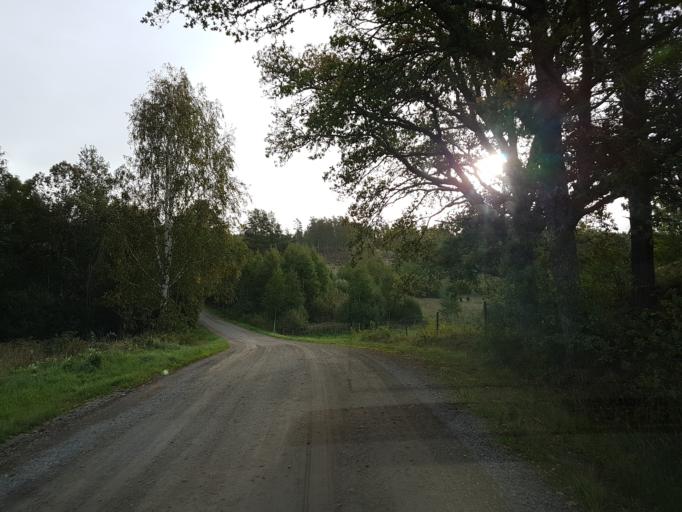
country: SE
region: OEstergoetland
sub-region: Atvidabergs Kommun
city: Atvidaberg
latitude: 58.2121
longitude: 16.0201
